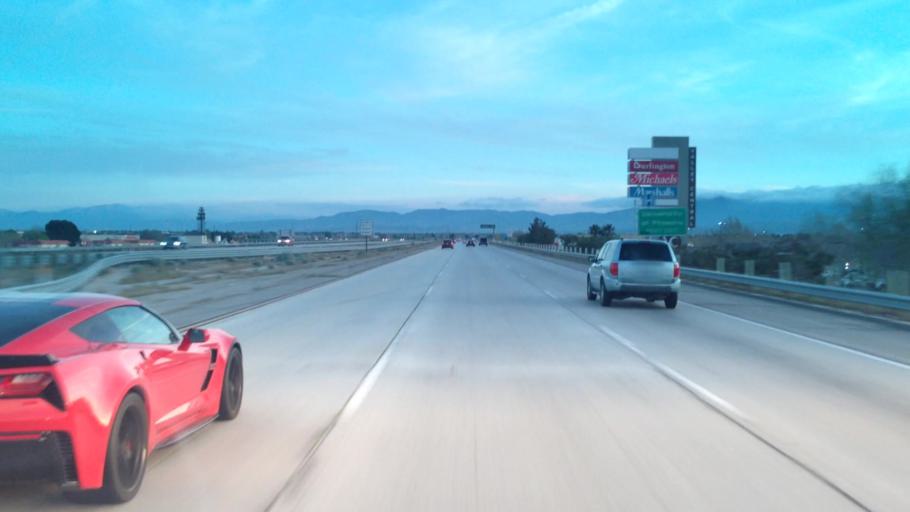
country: US
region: California
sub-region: Los Angeles County
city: Lancaster
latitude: 34.6966
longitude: -118.1667
